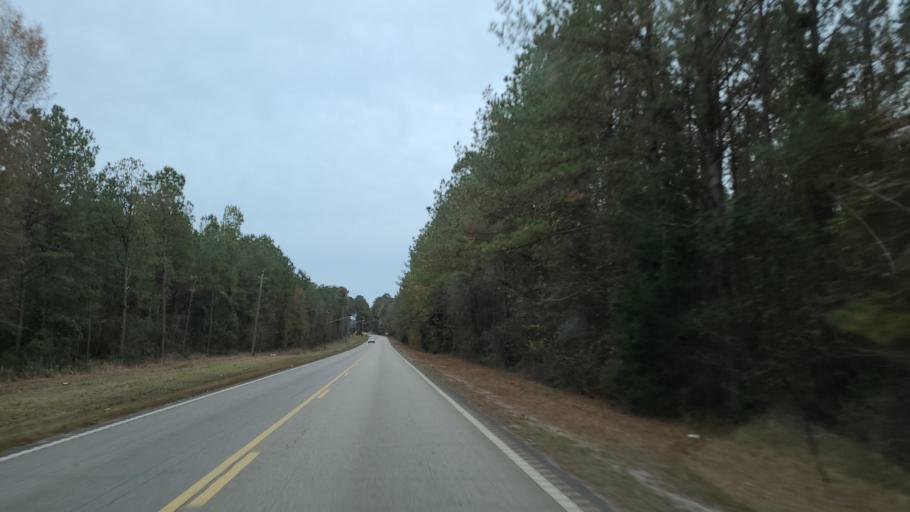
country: US
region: Mississippi
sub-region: Clarke County
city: Stonewall
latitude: 32.0526
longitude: -88.8973
